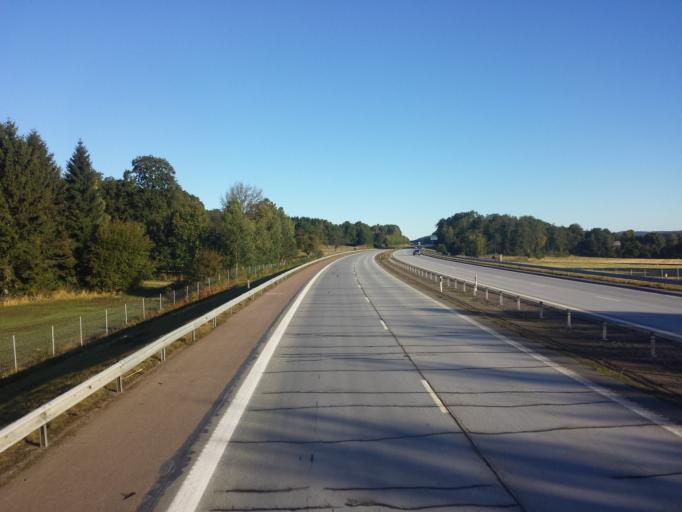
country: SE
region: Halland
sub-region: Halmstads Kommun
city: Getinge
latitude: 56.8220
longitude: 12.7104
